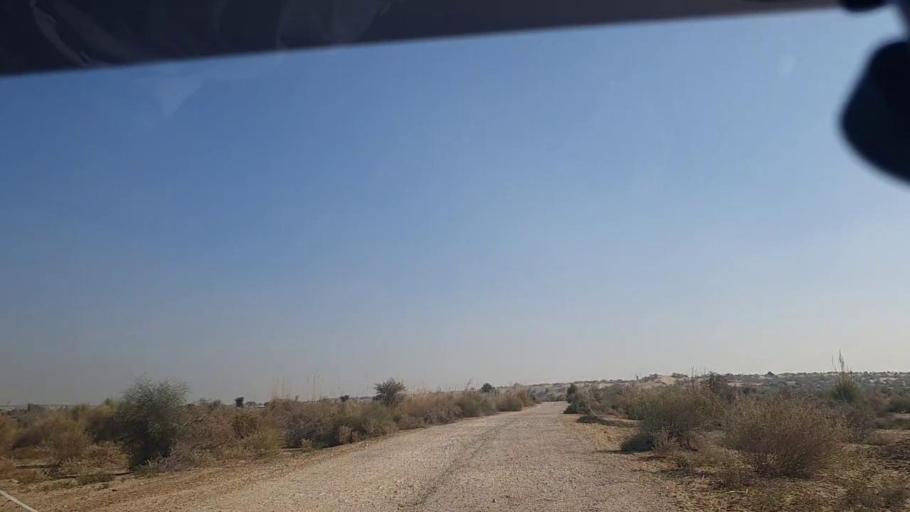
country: PK
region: Sindh
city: Khanpur
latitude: 27.5616
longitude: 69.3238
